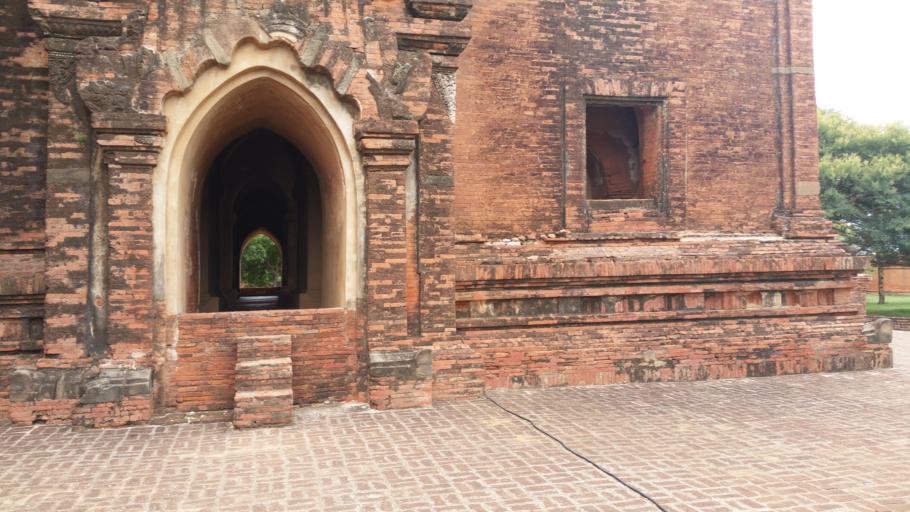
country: MM
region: Magway
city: Chauk
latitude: 21.1618
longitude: 94.8732
